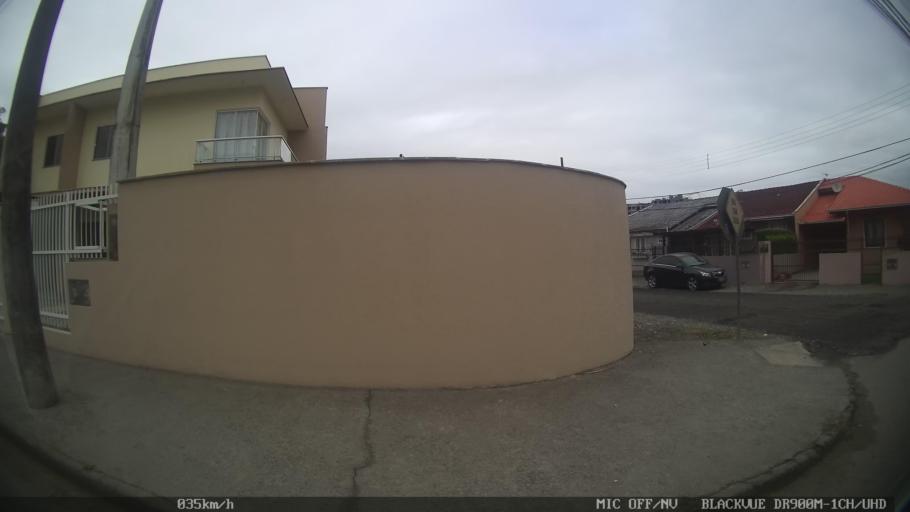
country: BR
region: Santa Catarina
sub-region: Joinville
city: Joinville
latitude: -26.2671
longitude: -48.8903
